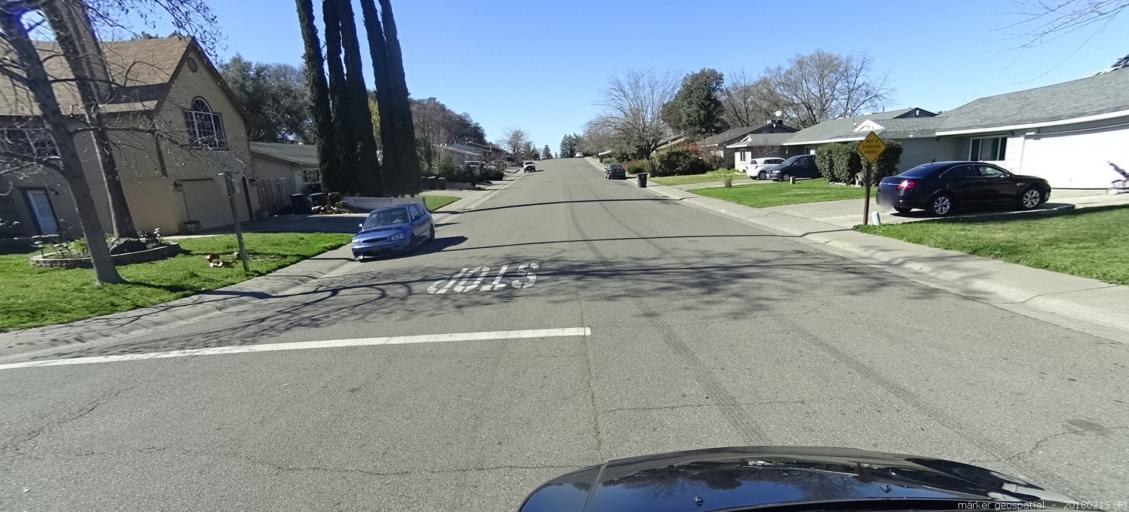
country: US
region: California
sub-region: Sacramento County
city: Fair Oaks
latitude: 38.6712
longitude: -121.3019
